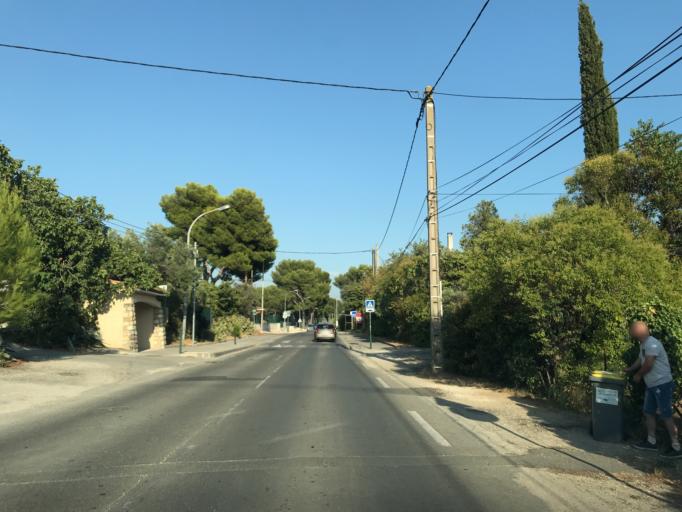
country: FR
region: Provence-Alpes-Cote d'Azur
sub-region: Departement des Bouches-du-Rhone
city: La Fare-les-Oliviers
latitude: 43.5506
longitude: 5.2097
